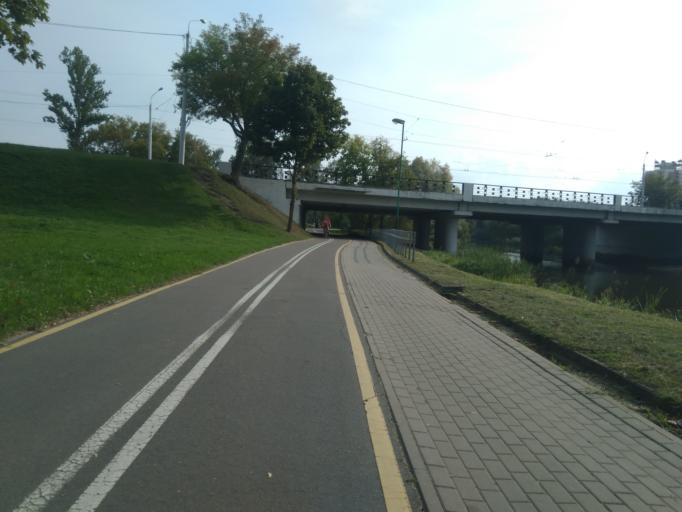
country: BY
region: Minsk
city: Minsk
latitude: 53.8748
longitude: 27.5844
